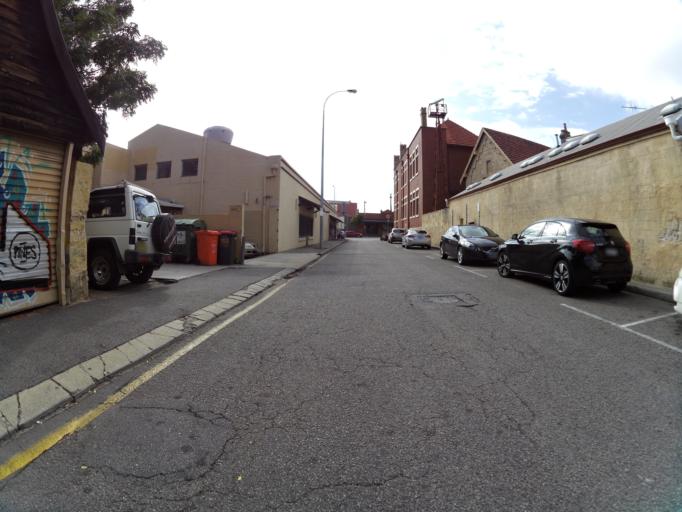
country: AU
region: Western Australia
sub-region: Fremantle
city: South Fremantle
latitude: -32.0569
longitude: 115.7487
